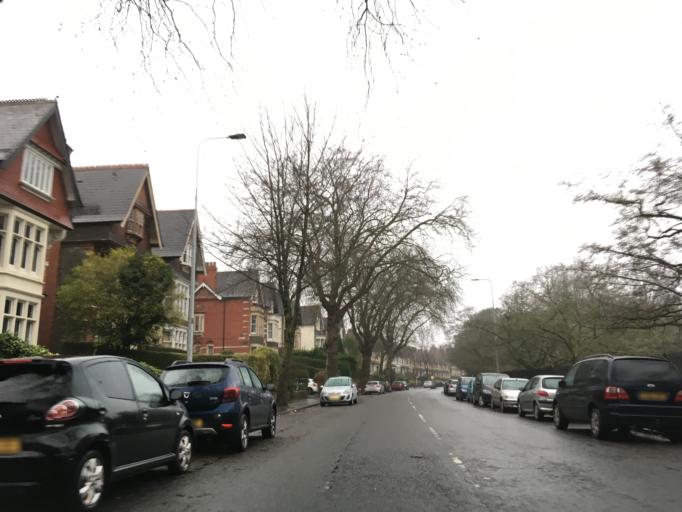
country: GB
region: Wales
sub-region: Cardiff
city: Cardiff
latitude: 51.4998
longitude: -3.1721
